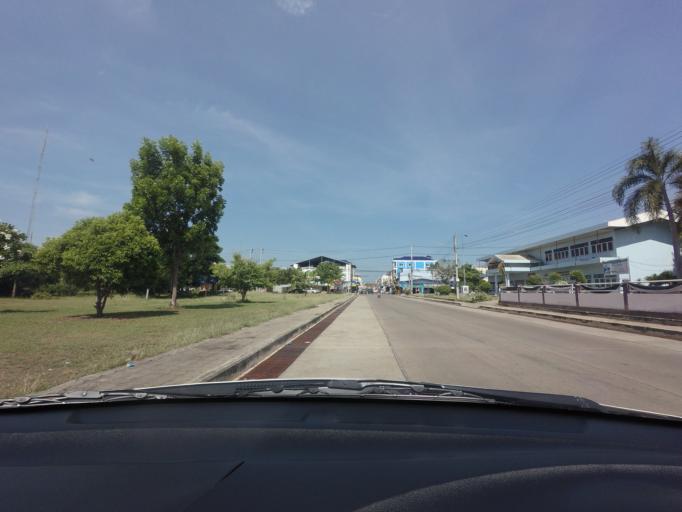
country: TH
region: Suphan Buri
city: Dan Chang
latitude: 14.8414
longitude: 99.6957
